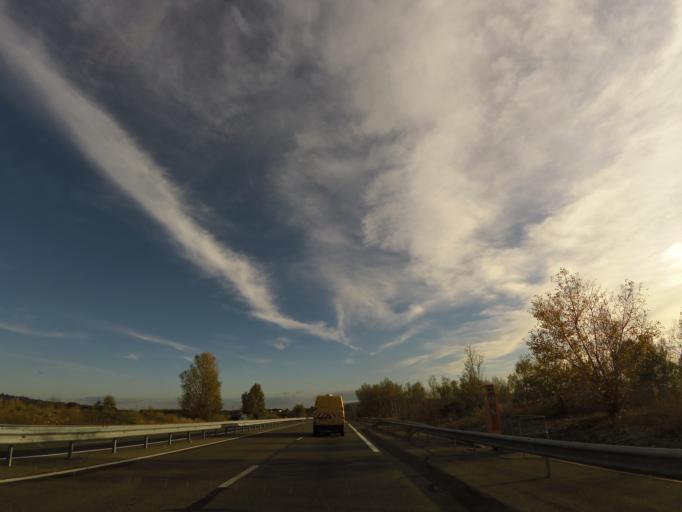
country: FR
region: Languedoc-Roussillon
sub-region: Departement du Gard
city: Vezenobres
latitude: 44.0363
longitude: 4.1445
